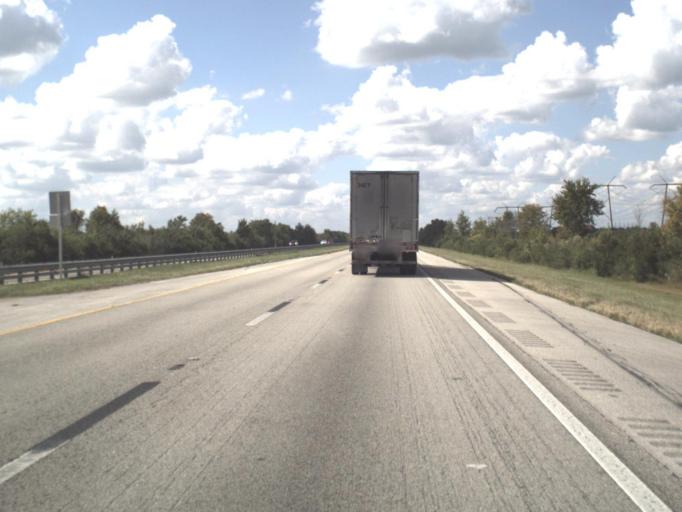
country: US
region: Florida
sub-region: Indian River County
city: Fellsmere
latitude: 27.5595
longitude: -80.7516
